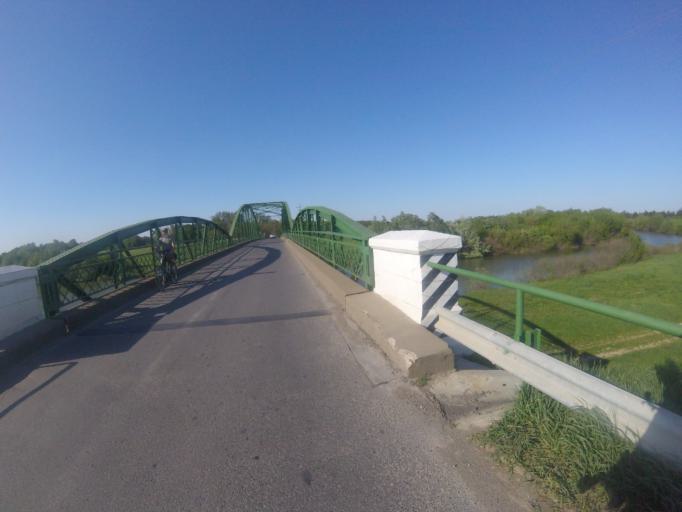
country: HU
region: Bekes
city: Gyula
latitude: 46.6999
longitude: 21.3128
